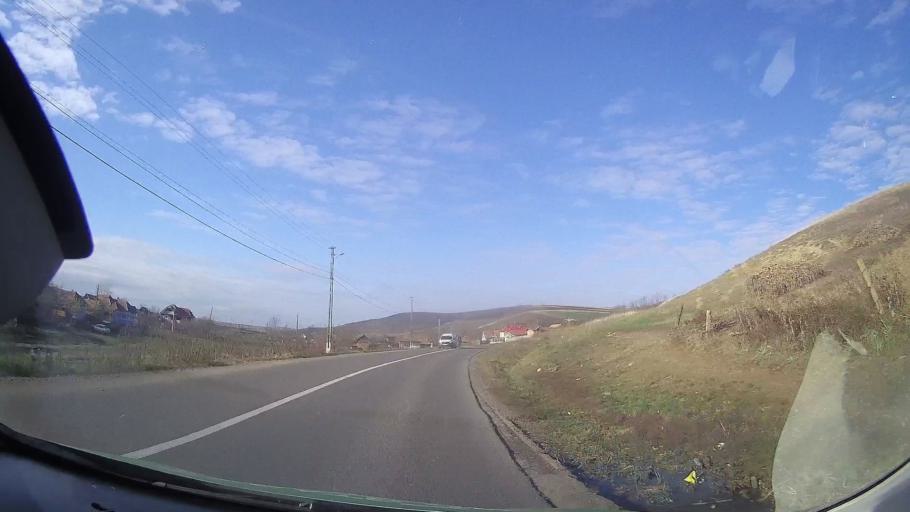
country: RO
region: Mures
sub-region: Comuna Grebenisu de Campie
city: Grebenisu de Campie
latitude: 46.6083
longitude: 24.2845
